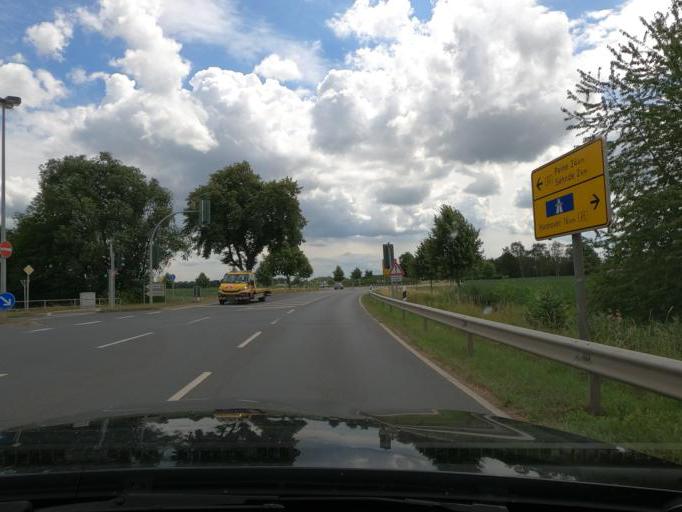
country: DE
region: Lower Saxony
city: Sehnde
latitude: 52.3317
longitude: 9.9491
